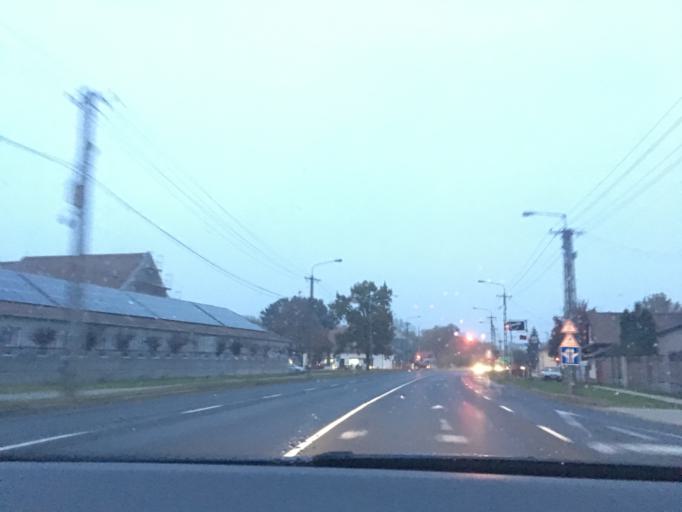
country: HU
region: Pest
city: Pilis
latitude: 47.2870
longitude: 19.5456
